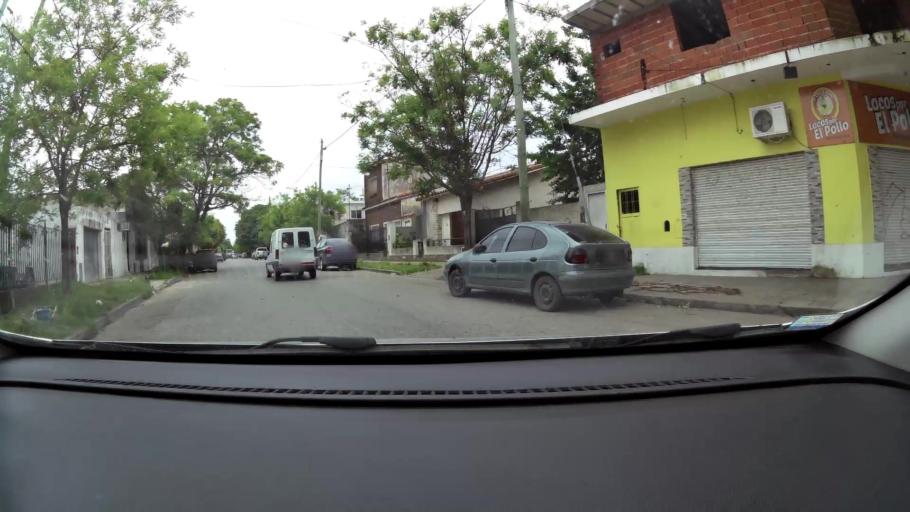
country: AR
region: Buenos Aires
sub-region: Partido de Zarate
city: Zarate
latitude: -34.1035
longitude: -59.0192
